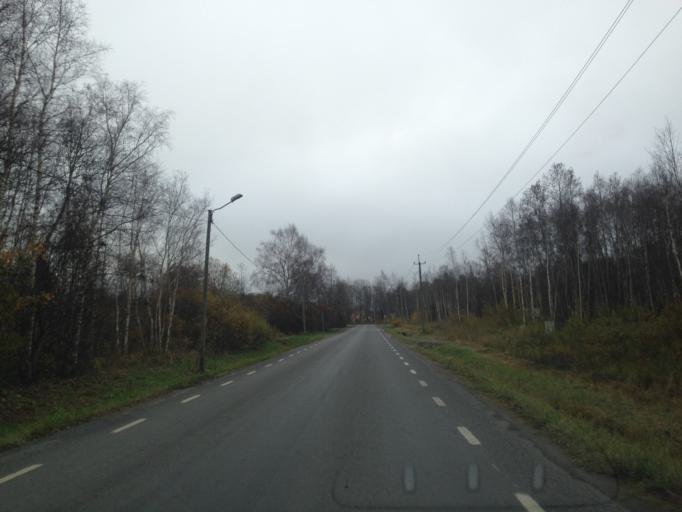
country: EE
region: Harju
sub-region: Harku vald
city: Tabasalu
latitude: 59.3756
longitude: 24.5398
